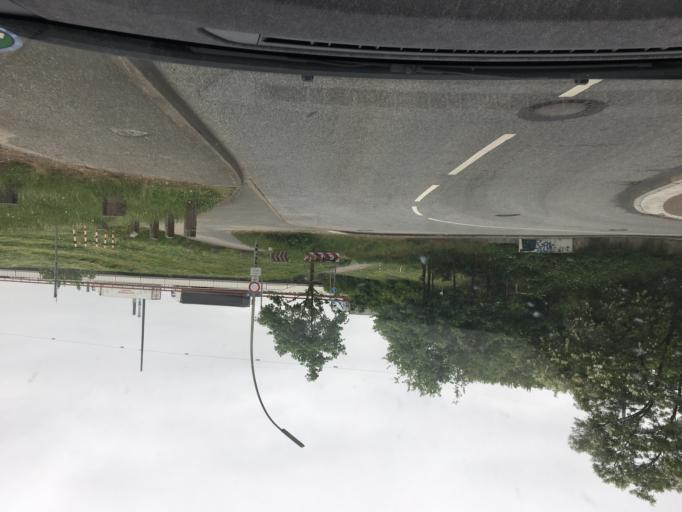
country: DE
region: Hamburg
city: Rothenburgsort
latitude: 53.5229
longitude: 10.0219
